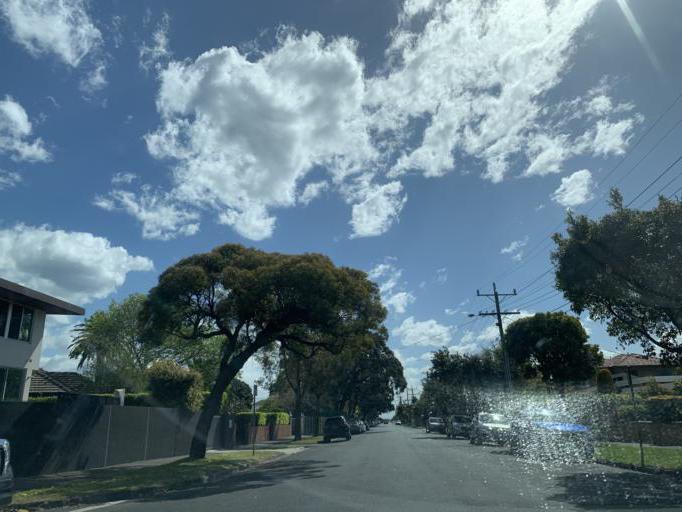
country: AU
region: Victoria
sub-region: Bayside
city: North Brighton
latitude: -37.9130
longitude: 144.9903
